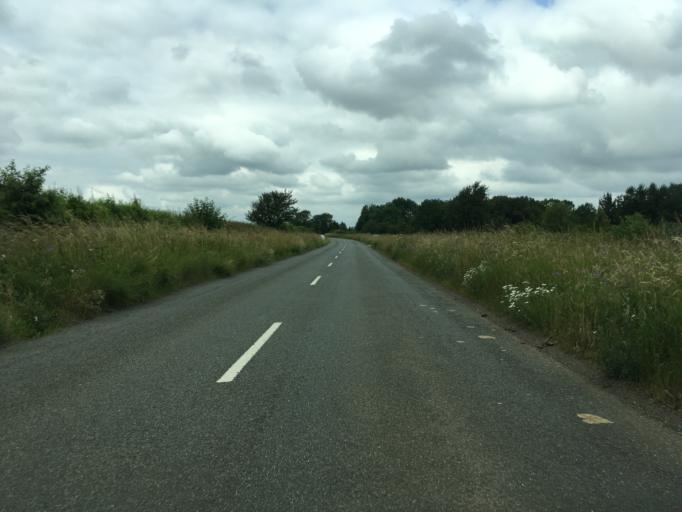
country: GB
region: England
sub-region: Oxfordshire
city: Chipping Norton
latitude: 51.9188
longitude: -1.5016
